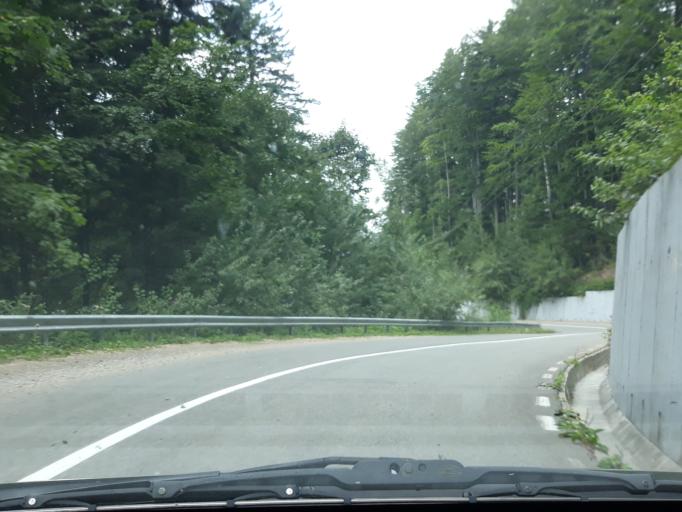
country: RO
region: Bihor
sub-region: Comuna Pietroasa
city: Pietroasa
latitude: 46.5920
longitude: 22.6725
